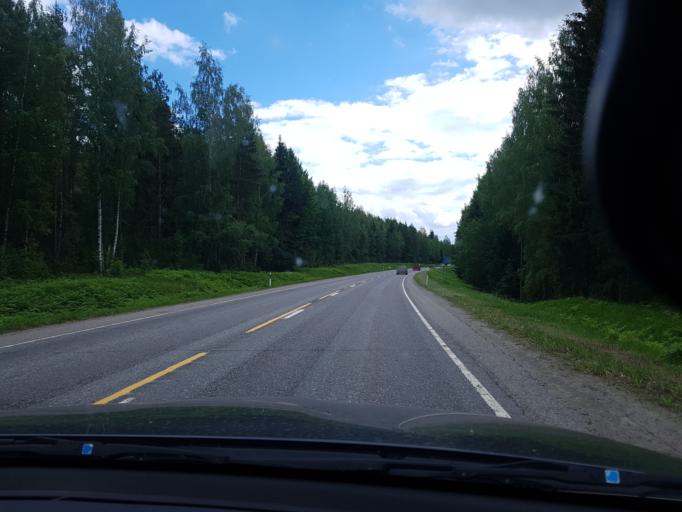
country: FI
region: Pirkanmaa
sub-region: Tampere
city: Paelkaene
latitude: 61.3077
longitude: 24.2952
